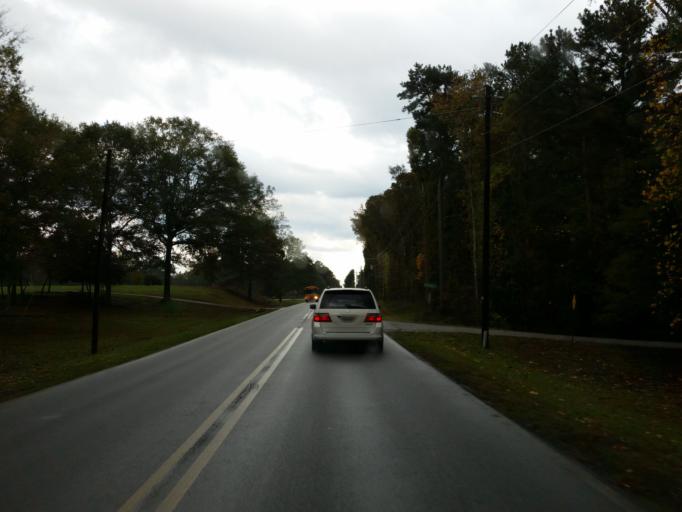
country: US
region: Georgia
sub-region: Henry County
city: Stockbridge
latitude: 33.4885
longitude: -84.2452
